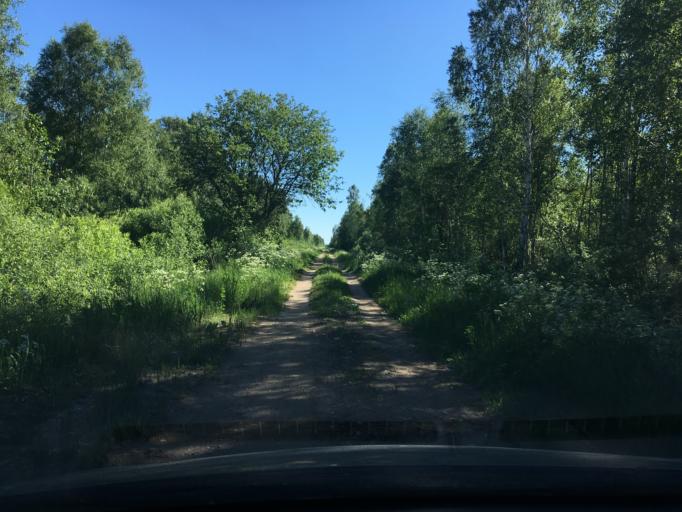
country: EE
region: Laeaene
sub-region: Lihula vald
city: Lihula
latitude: 58.6308
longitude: 23.7409
